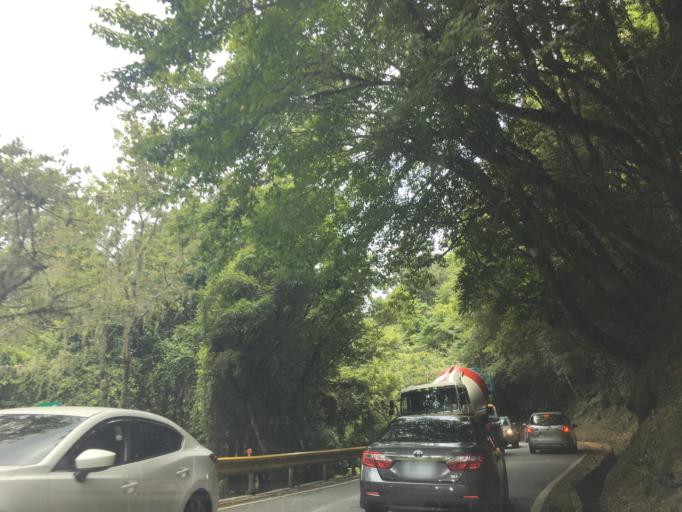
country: TW
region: Taiwan
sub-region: Hualien
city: Hualian
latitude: 24.1768
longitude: 121.3865
